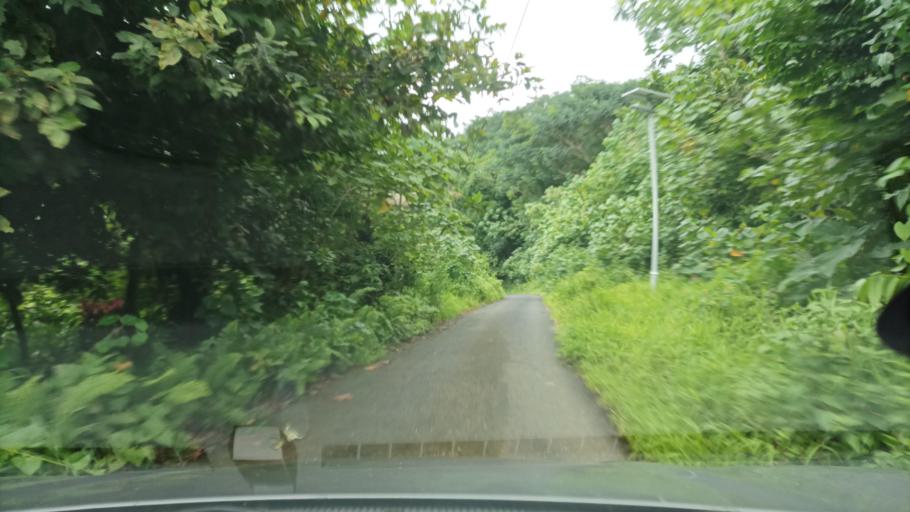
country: FM
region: Pohnpei
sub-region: Kolonia Municipality
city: Kolonia
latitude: 6.9410
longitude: 158.2717
